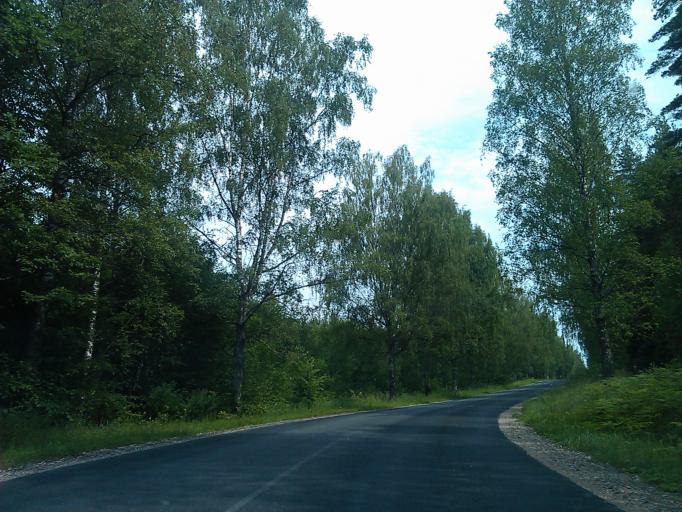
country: LV
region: Priekuli
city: Priekuli
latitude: 57.3673
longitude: 25.3815
